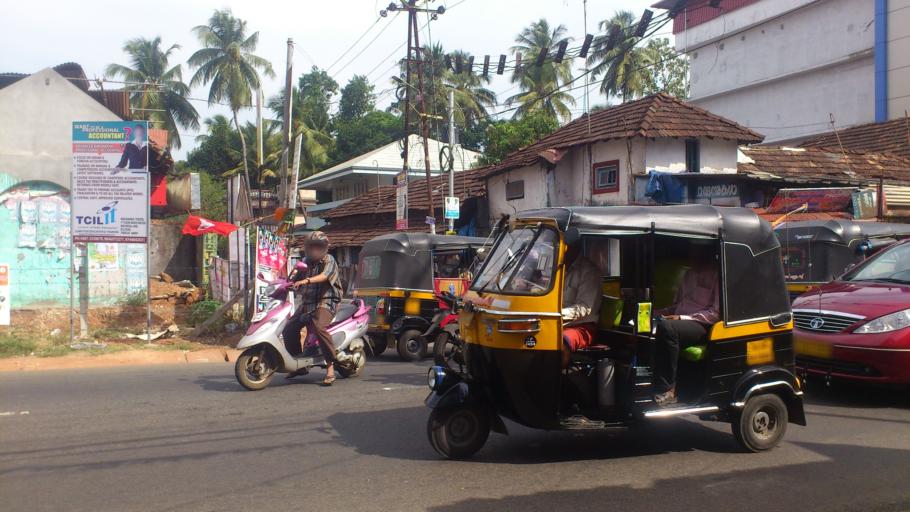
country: IN
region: Kerala
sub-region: Thrissur District
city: Trichur
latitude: 10.5233
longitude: 76.2073
